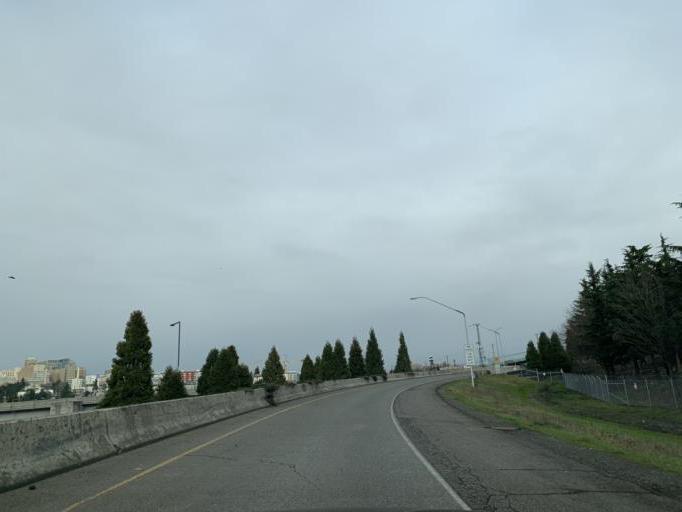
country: US
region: Washington
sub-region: King County
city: Seattle
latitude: 47.5930
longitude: -122.3200
